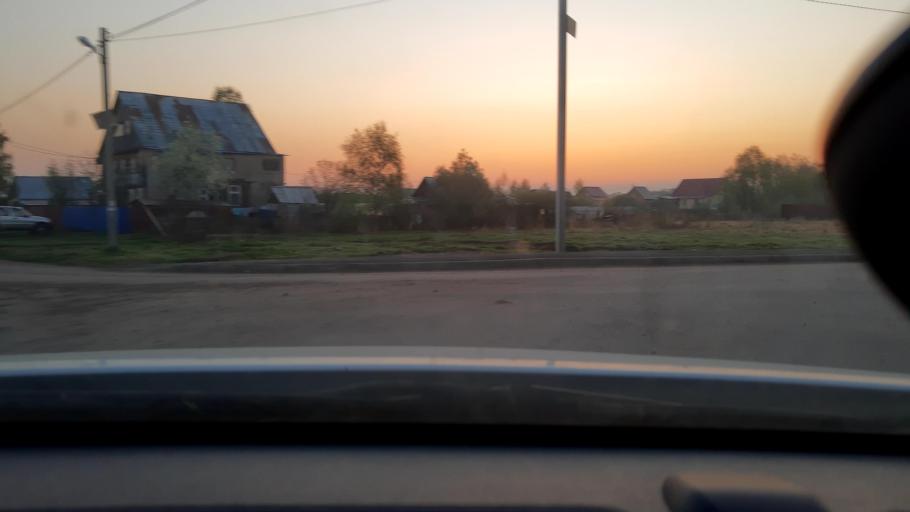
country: RU
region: Bashkortostan
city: Iglino
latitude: 54.8009
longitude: 56.2983
